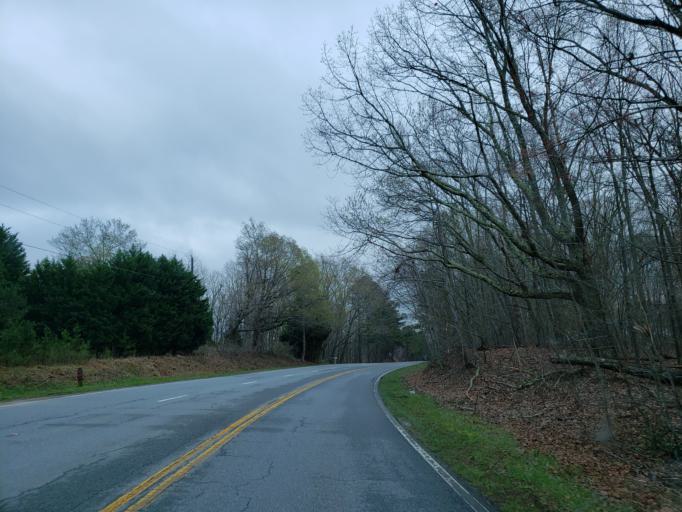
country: US
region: Georgia
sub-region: Polk County
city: Rockmart
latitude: 33.9232
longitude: -84.9705
